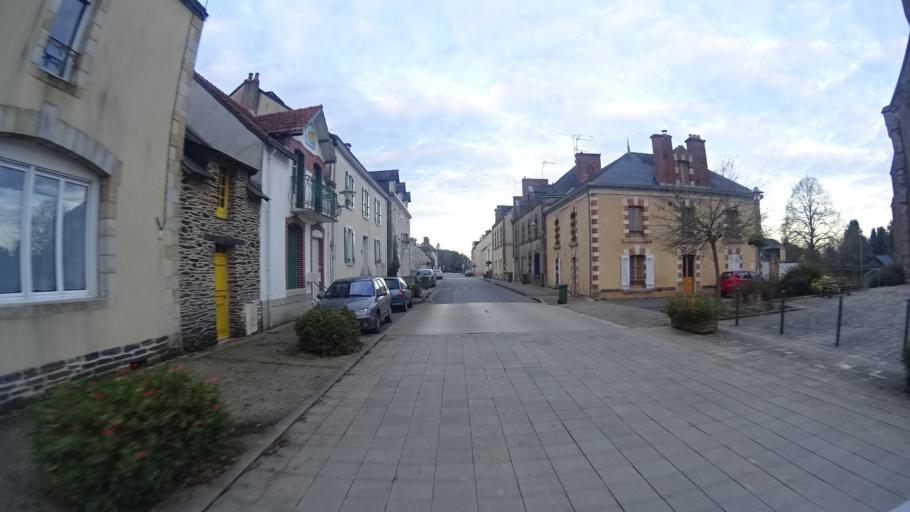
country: FR
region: Pays de la Loire
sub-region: Departement de la Loire-Atlantique
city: Avessac
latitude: 47.6727
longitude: -1.9141
